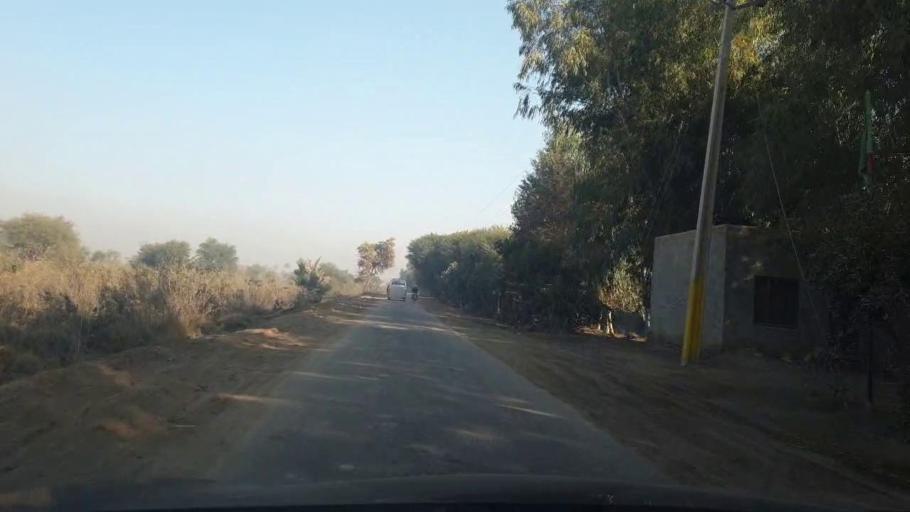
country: PK
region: Sindh
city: Mirpur Mathelo
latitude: 28.0669
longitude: 69.4657
